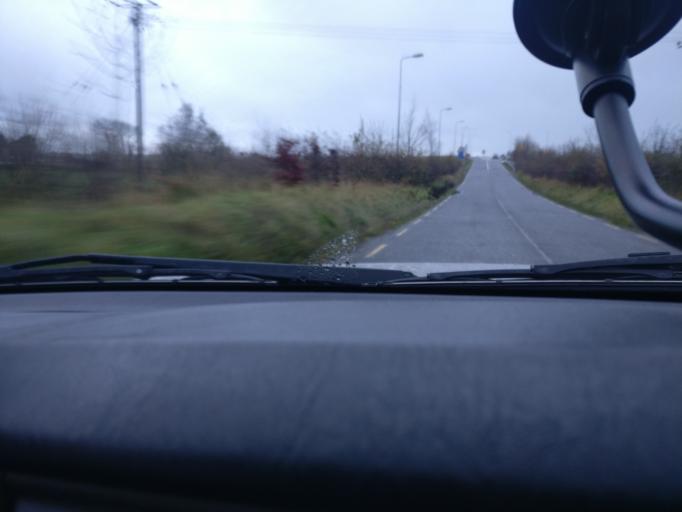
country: IE
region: Leinster
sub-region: An Iarmhi
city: Kinnegad
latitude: 53.4516
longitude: -7.1232
